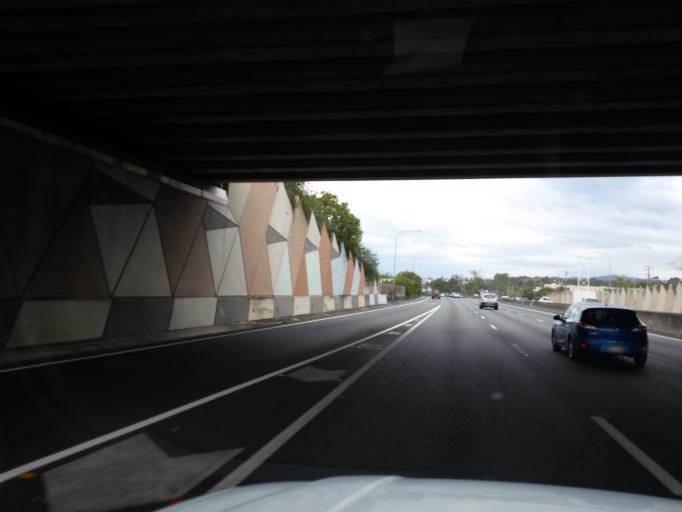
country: AU
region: Queensland
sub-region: Gold Coast
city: Nerang
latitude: -27.9965
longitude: 153.3400
